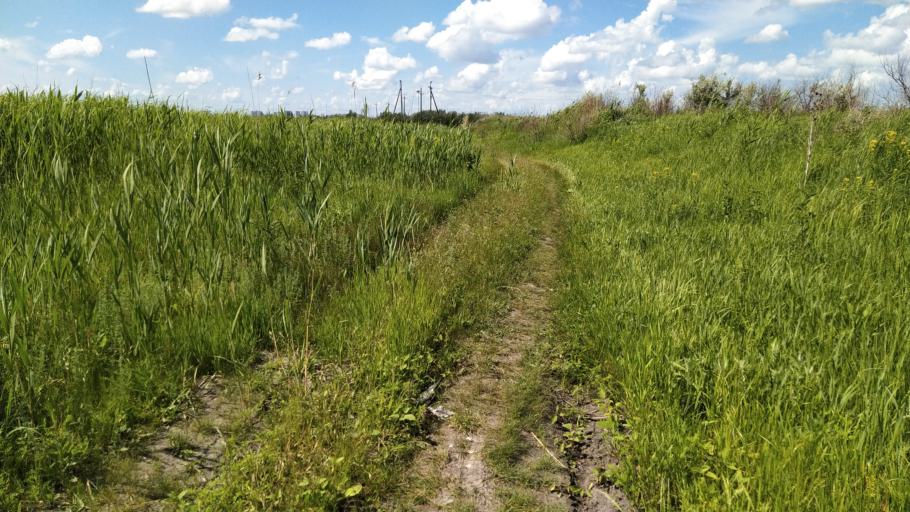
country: RU
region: Rostov
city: Bataysk
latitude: 47.1399
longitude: 39.6692
